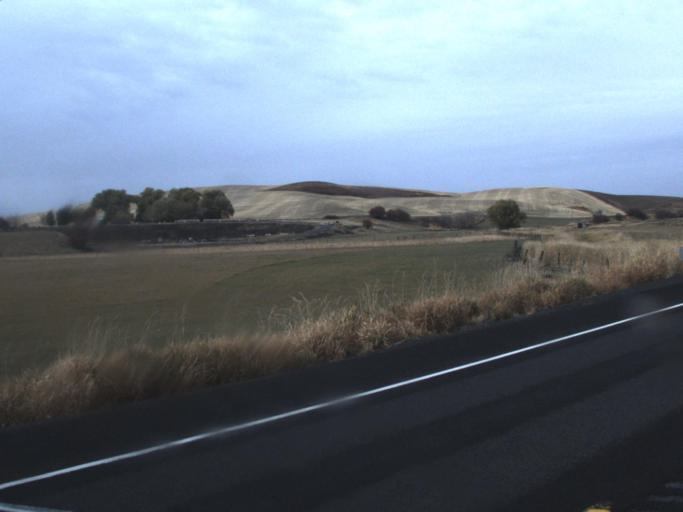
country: US
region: Washington
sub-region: Whitman County
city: Pullman
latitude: 46.5757
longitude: -117.1491
